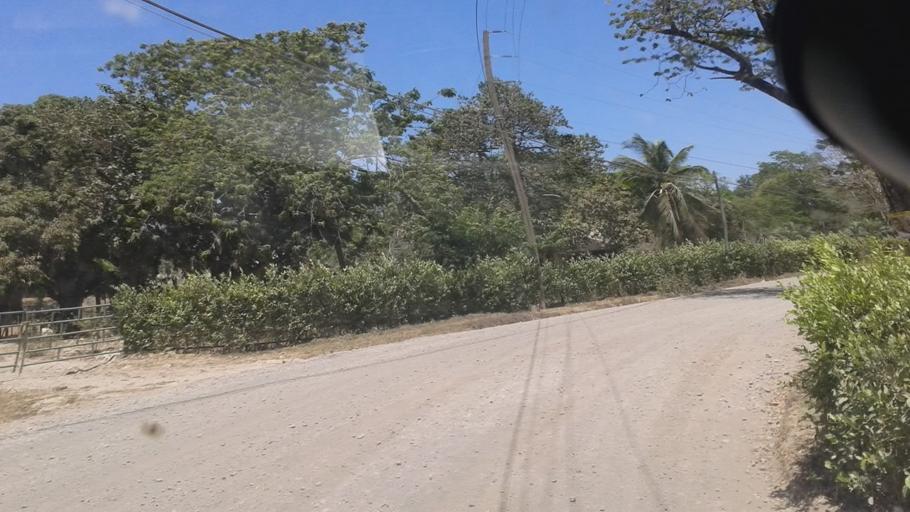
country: CR
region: Guanacaste
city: Samara
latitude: 9.9976
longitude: -85.6962
